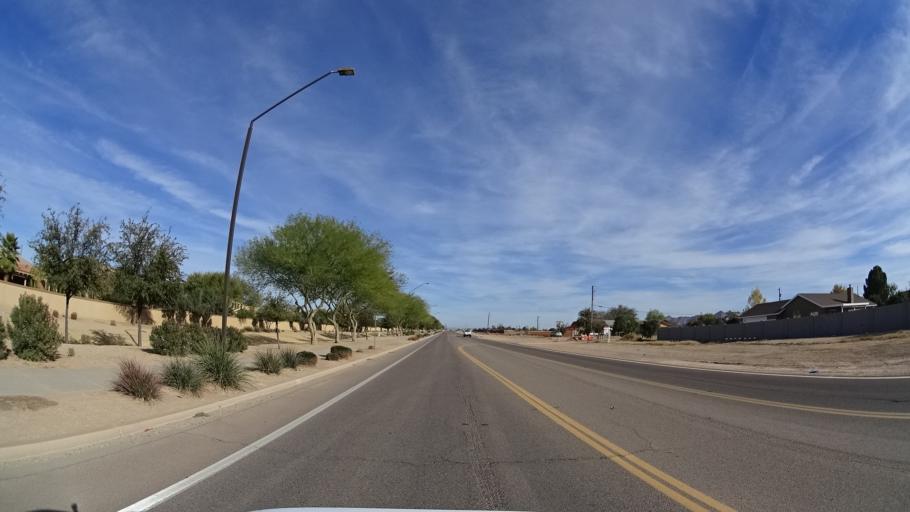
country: US
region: Arizona
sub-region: Maricopa County
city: Queen Creek
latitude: 33.2194
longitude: -111.7008
